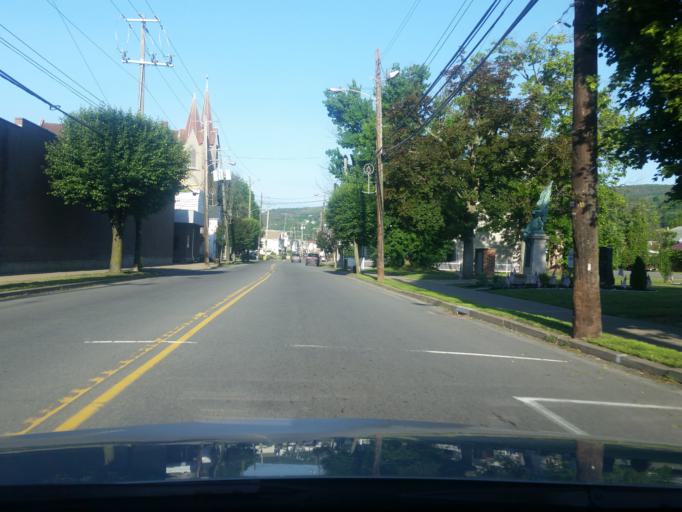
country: US
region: Pennsylvania
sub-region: Luzerne County
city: Plymouth
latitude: 41.2397
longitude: -75.9486
